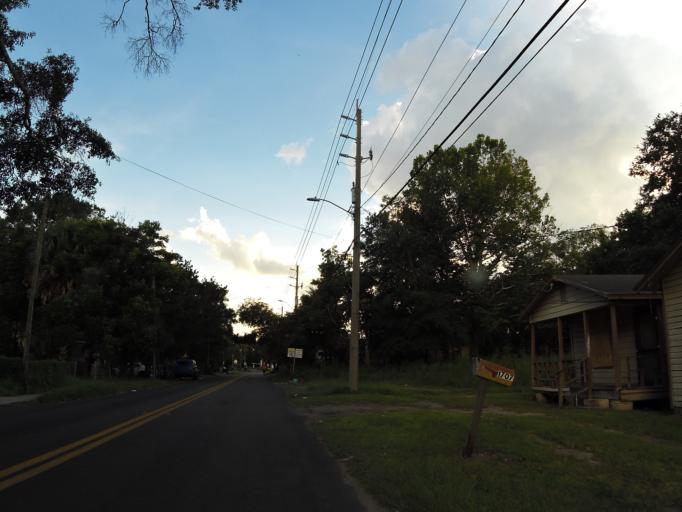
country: US
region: Florida
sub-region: Duval County
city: Jacksonville
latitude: 30.3393
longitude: -81.6868
